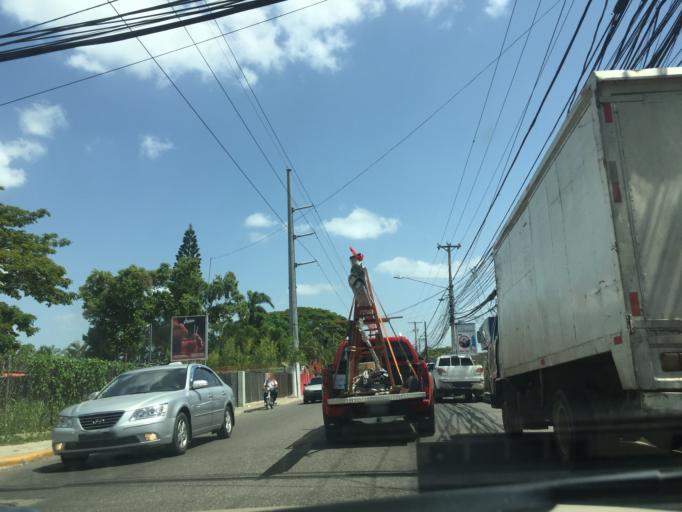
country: DO
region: Santiago
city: Santiago de los Caballeros
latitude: 19.4509
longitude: -70.6657
